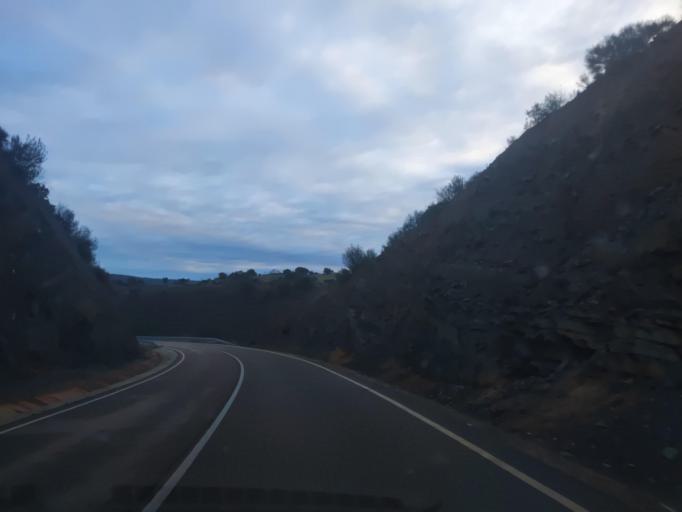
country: ES
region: Castille and Leon
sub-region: Provincia de Salamanca
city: Castillejo de Martin Viejo
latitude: 40.7073
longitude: -6.6402
